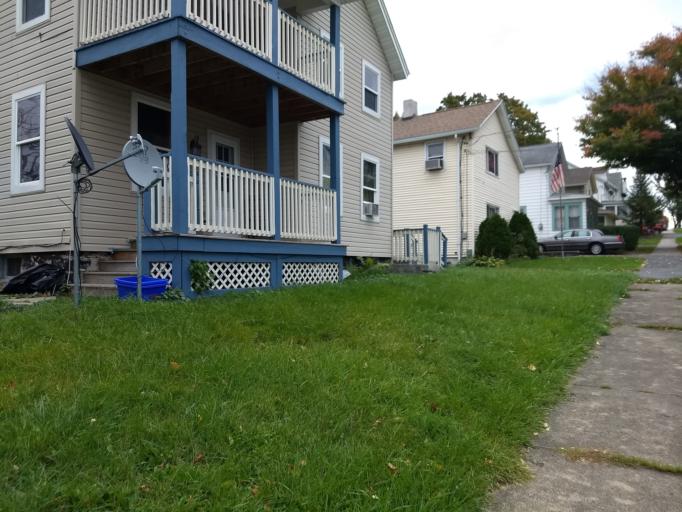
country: US
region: New York
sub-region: Onondaga County
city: Mattydale
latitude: 43.0809
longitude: -76.1547
